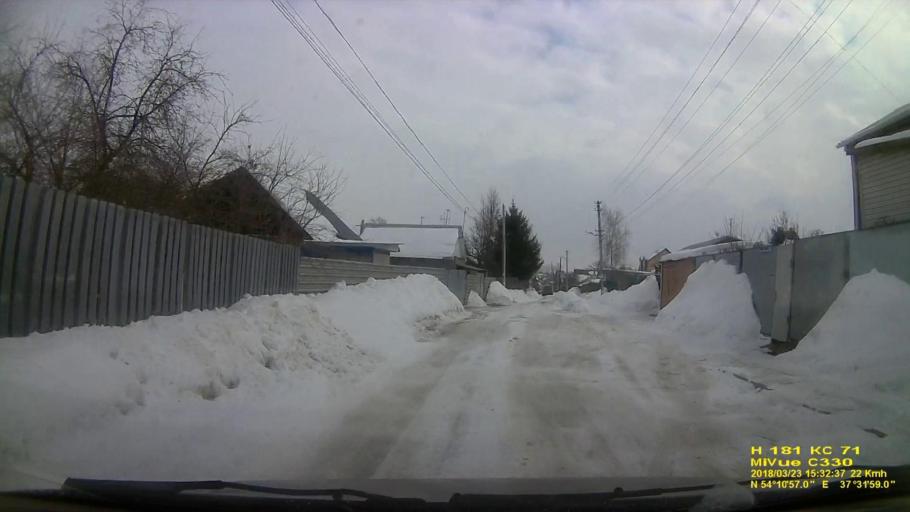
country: RU
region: Tula
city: Kosaya Gora
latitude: 54.1824
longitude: 37.5331
